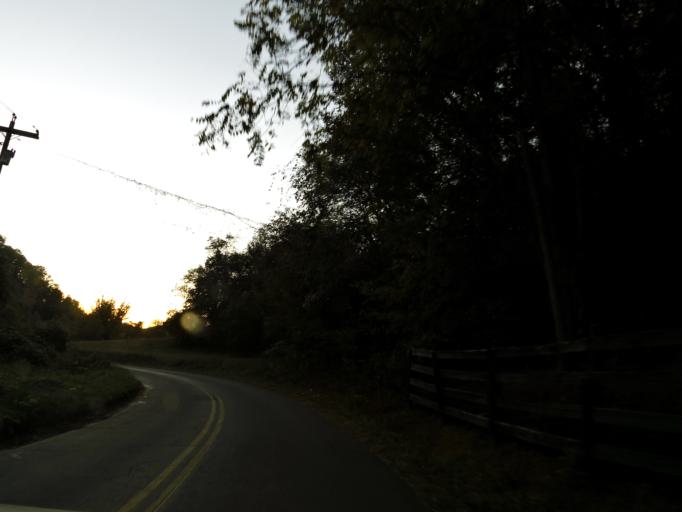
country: US
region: Tennessee
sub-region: Blount County
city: Wildwood
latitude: 35.7707
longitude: -83.8102
